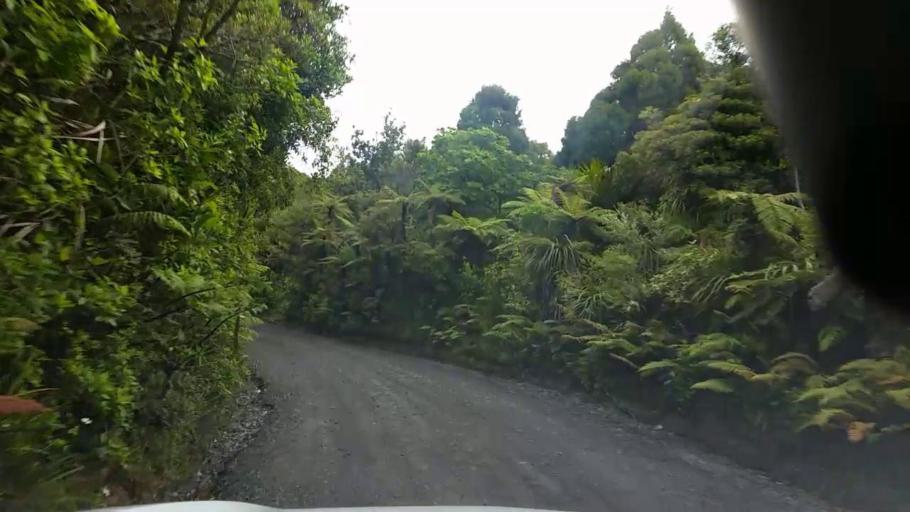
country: NZ
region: Auckland
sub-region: Auckland
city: Titirangi
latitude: -36.9419
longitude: 174.5244
